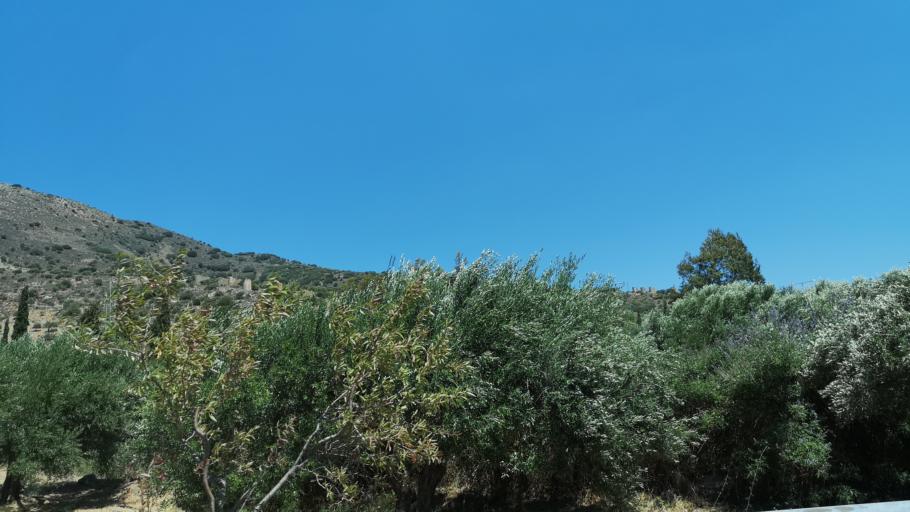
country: GR
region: Crete
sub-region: Nomos Lasithiou
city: Neapoli
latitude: 35.2411
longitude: 25.6444
